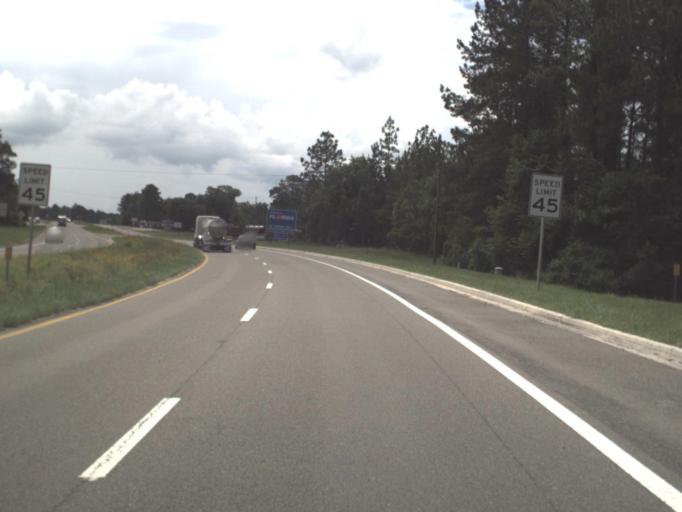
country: US
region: Georgia
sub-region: Charlton County
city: Folkston
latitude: 30.7739
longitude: -81.9785
